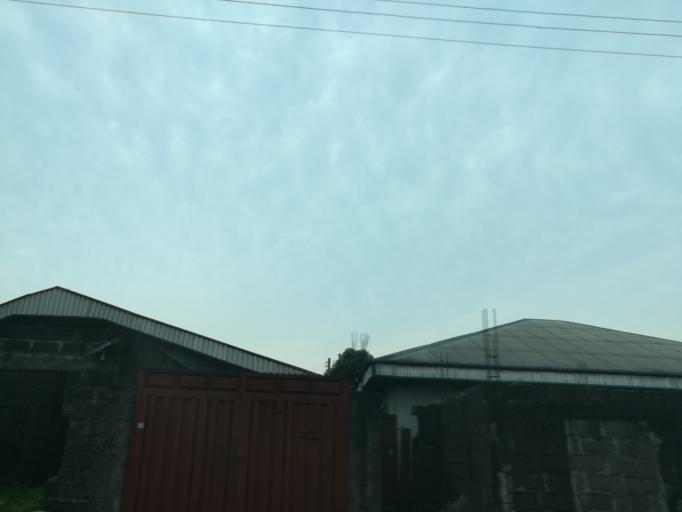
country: NG
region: Rivers
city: Port Harcourt
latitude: 4.8268
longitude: 7.0201
